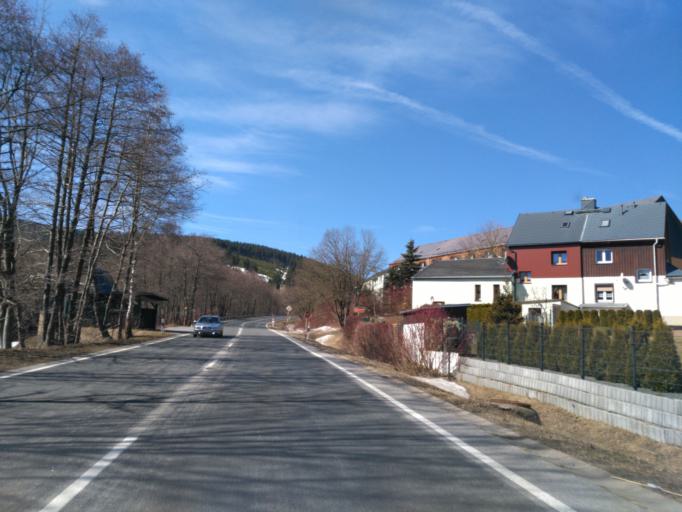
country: DE
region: Saxony
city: Kurort Oberwiesenthal
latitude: 50.4164
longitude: 12.9681
